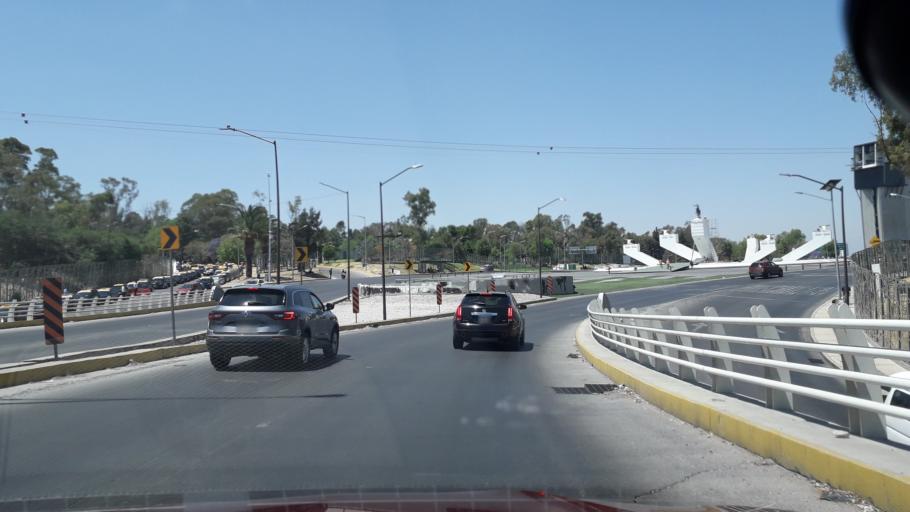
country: MX
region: Puebla
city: Puebla
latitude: 19.0610
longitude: -98.1830
